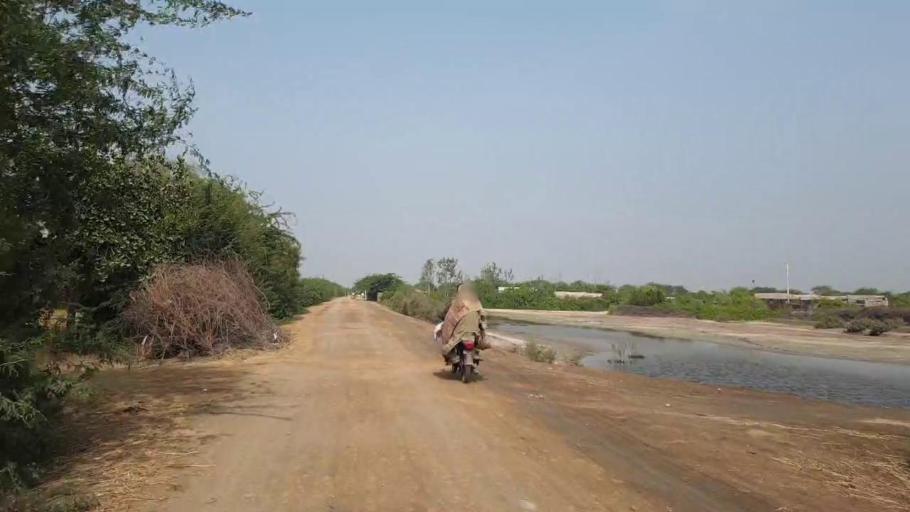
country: PK
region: Sindh
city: Kario
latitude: 24.7546
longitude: 68.5592
